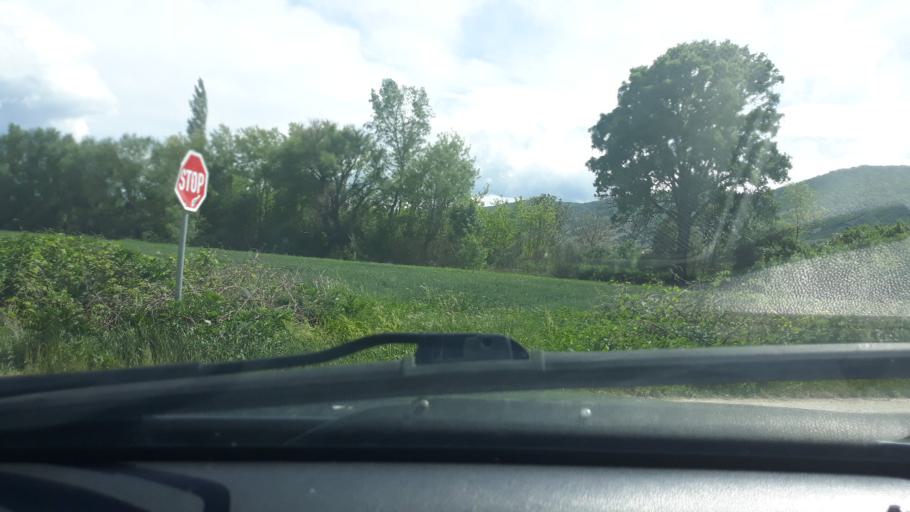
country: MK
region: Krivogastani
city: Krivogashtani
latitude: 41.3419
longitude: 21.3160
